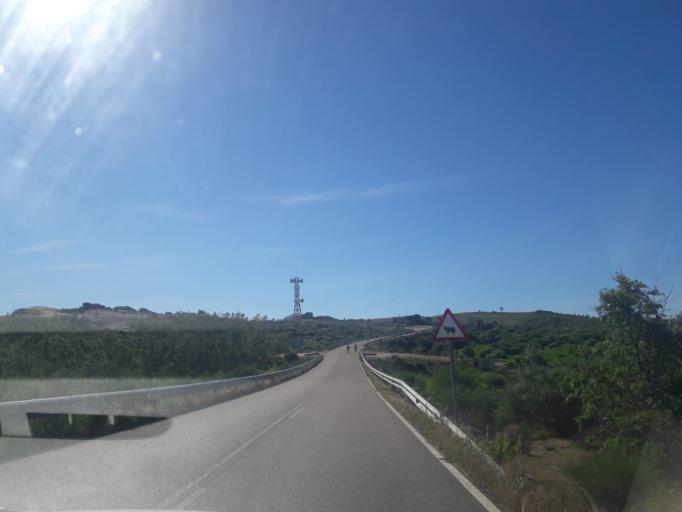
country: ES
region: Castille and Leon
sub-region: Provincia de Salamanca
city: Lagunilla
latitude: 40.3258
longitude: -5.9358
